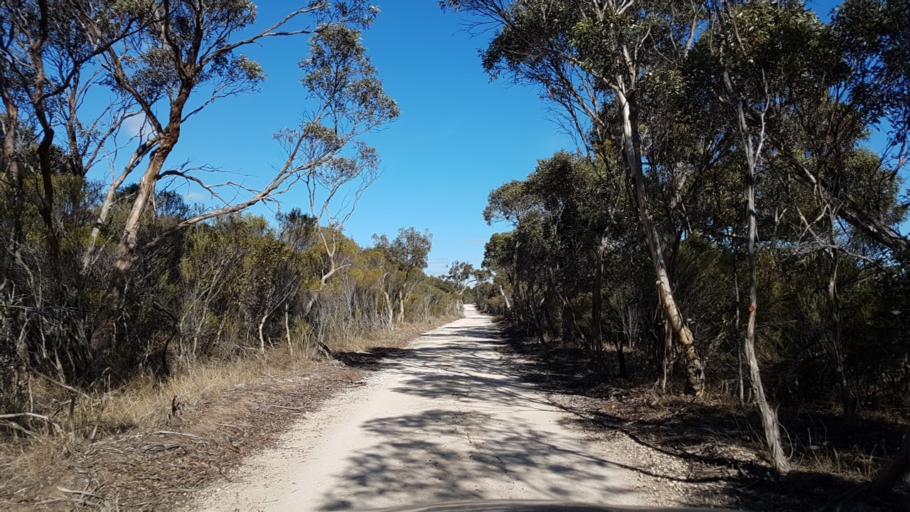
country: AU
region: South Australia
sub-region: Alexandrina
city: Strathalbyn
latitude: -35.3774
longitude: 138.8328
